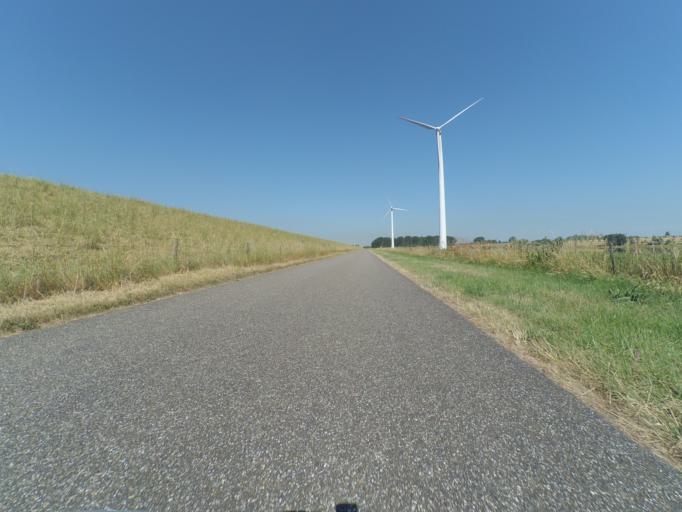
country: NL
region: North Brabant
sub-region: Gemeente Woensdrecht
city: Woensdrecht
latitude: 51.3976
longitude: 4.2253
